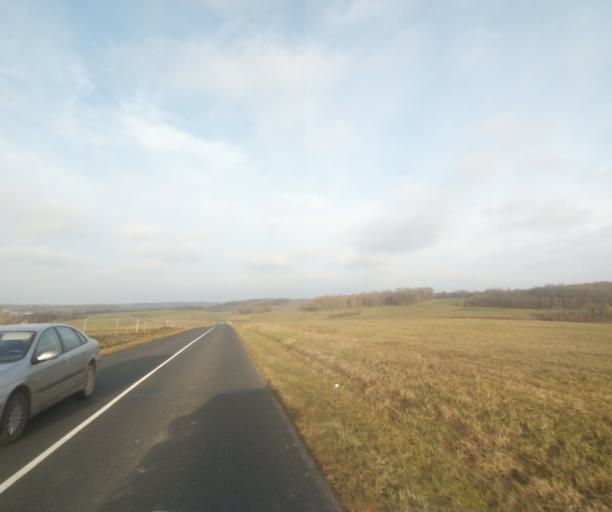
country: FR
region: Champagne-Ardenne
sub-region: Departement de la Marne
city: Sermaize-les-Bains
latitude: 48.7319
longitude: 4.9315
